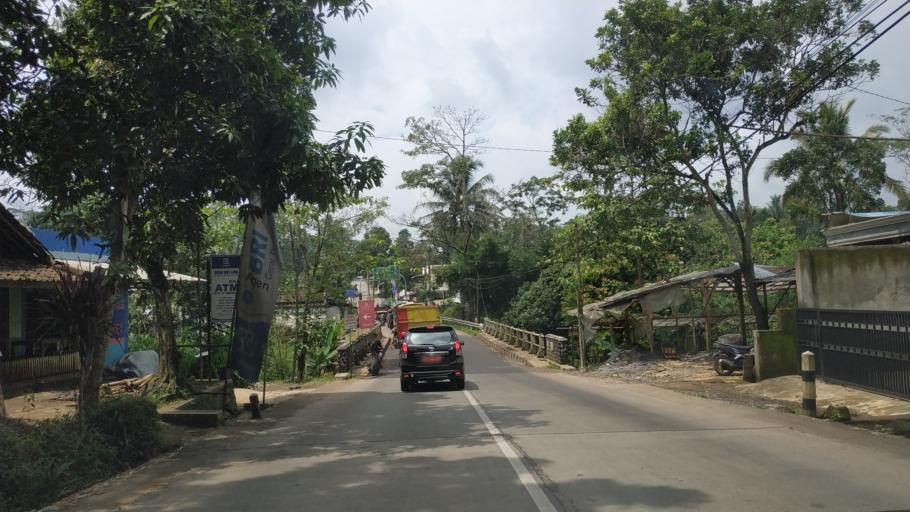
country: ID
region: Central Java
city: Weleri
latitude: -7.0981
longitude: 110.0620
